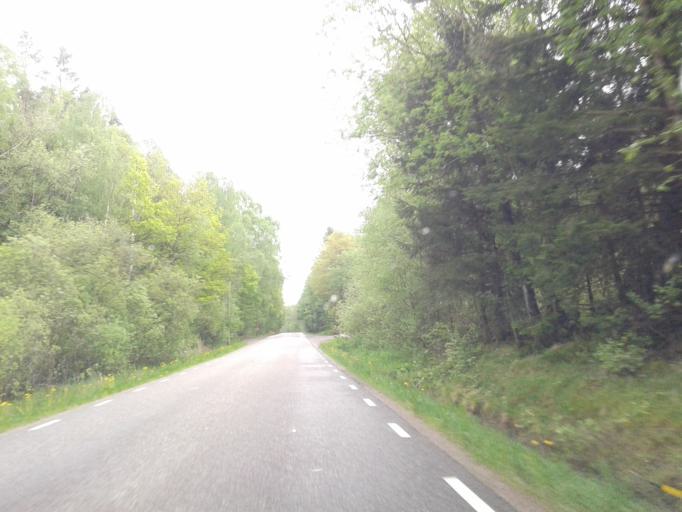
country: SE
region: Vaestra Goetaland
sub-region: Kungalvs Kommun
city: Kode
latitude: 57.8973
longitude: 11.8934
